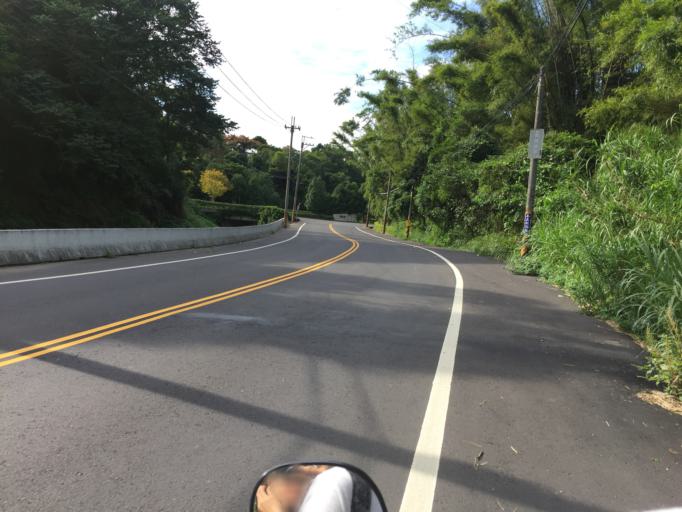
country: TW
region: Taiwan
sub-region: Hsinchu
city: Hsinchu
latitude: 24.7644
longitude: 120.9422
